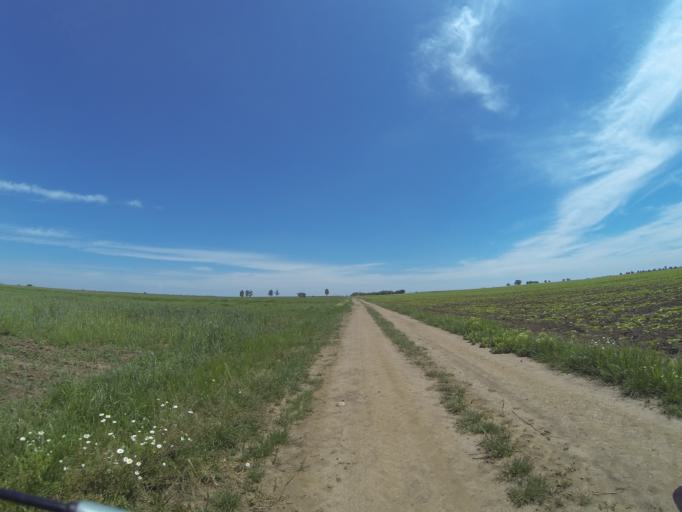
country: RO
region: Dolj
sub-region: Comuna Diosti
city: Radomir
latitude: 44.1468
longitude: 24.1557
